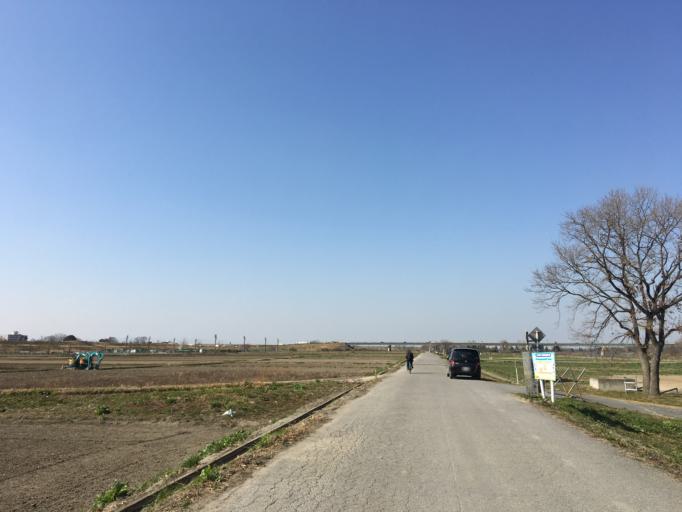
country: JP
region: Saitama
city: Shiki
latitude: 35.8490
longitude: 139.5939
